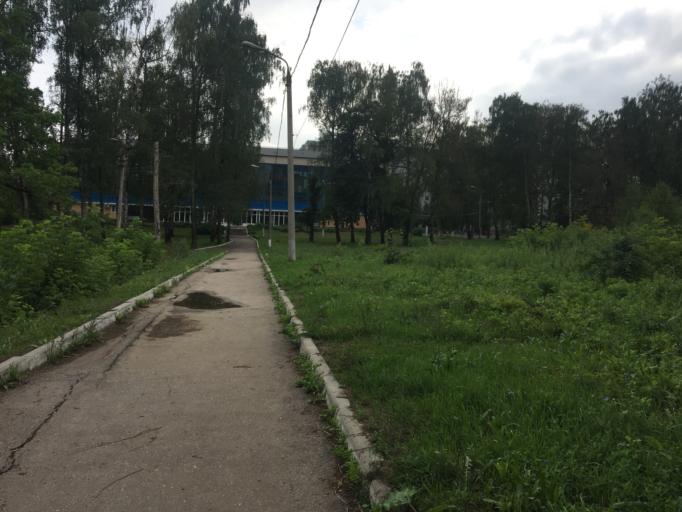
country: RU
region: Tula
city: Tula
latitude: 54.1731
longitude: 37.6036
